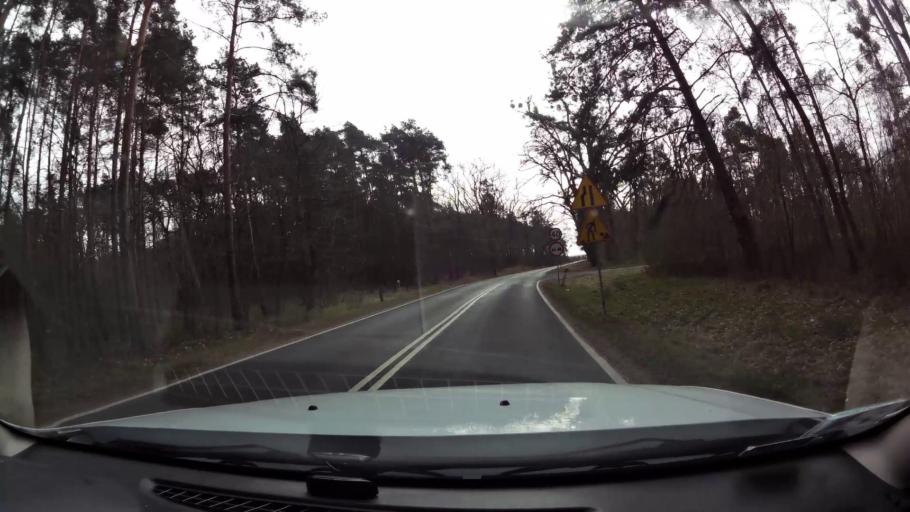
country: PL
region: West Pomeranian Voivodeship
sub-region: Powiat mysliborski
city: Debno
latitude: 52.7574
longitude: 14.6852
